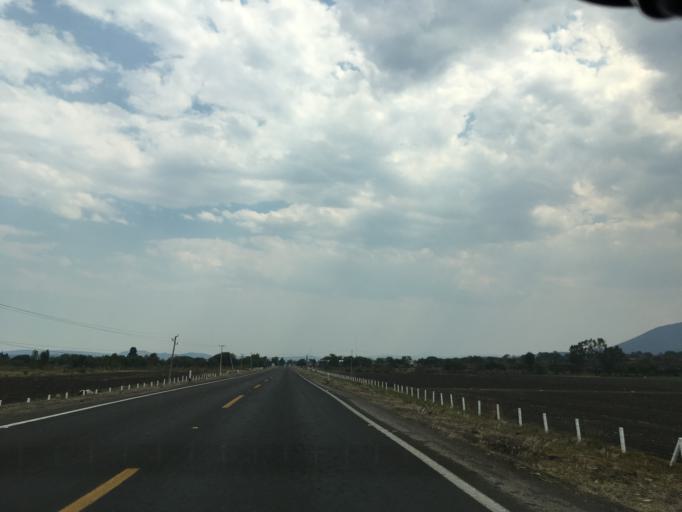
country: MX
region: Michoacan
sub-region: Cuitzeo
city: Cuamio
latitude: 20.0481
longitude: -101.1510
